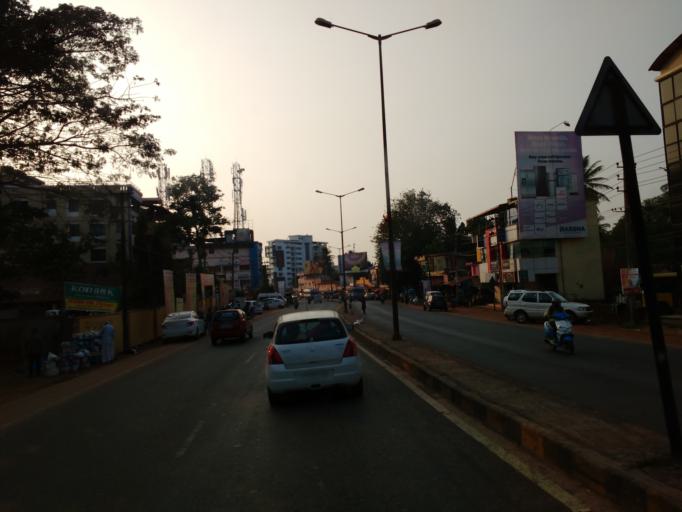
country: IN
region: Karnataka
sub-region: Dakshina Kannada
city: Mangalore
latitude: 12.8843
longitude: 74.8687
